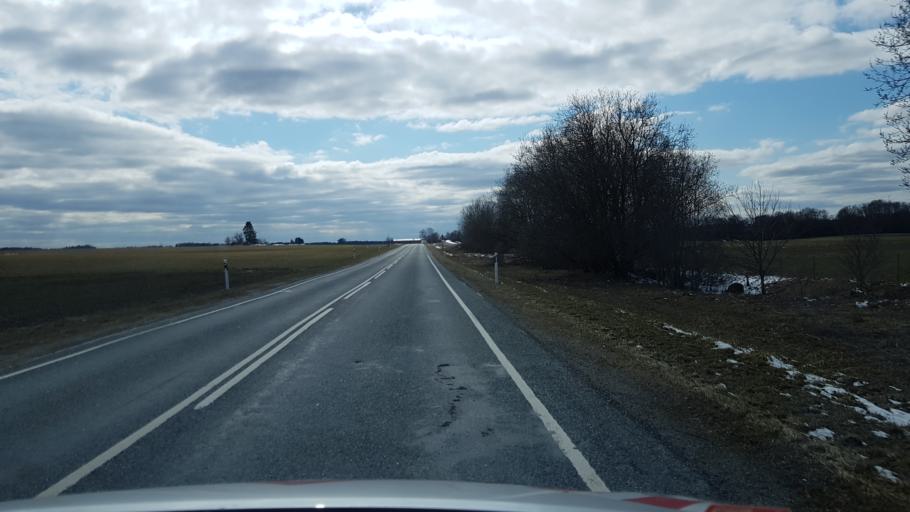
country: EE
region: Laeaene-Virumaa
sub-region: Tapa vald
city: Tapa
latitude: 59.3128
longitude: 26.0026
